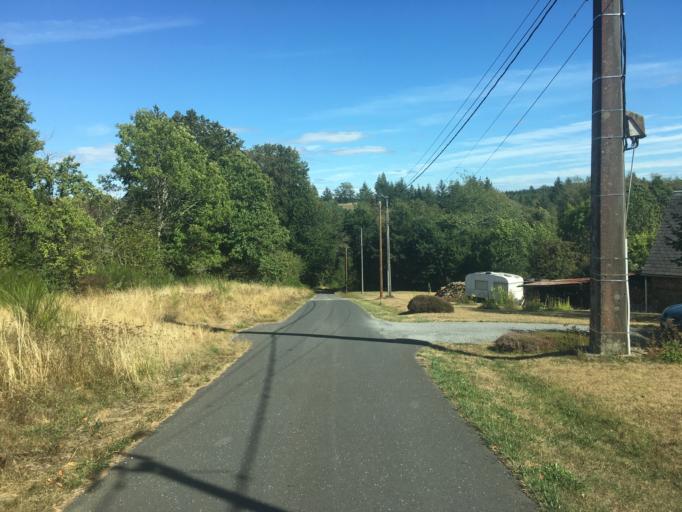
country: FR
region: Limousin
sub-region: Departement de la Correze
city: Meymac
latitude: 45.4256
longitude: 2.1592
